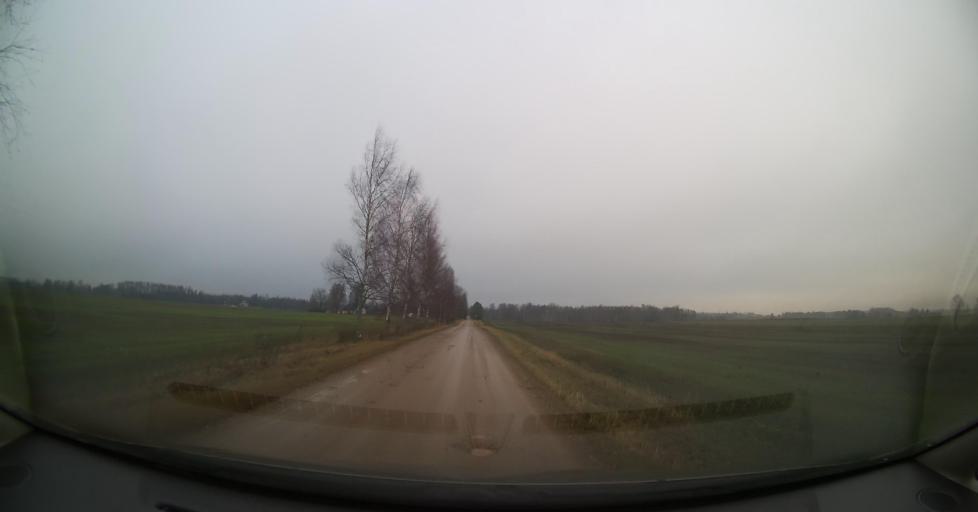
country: EE
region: Tartu
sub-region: Tartu linn
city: Tartu
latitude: 58.3858
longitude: 27.0240
